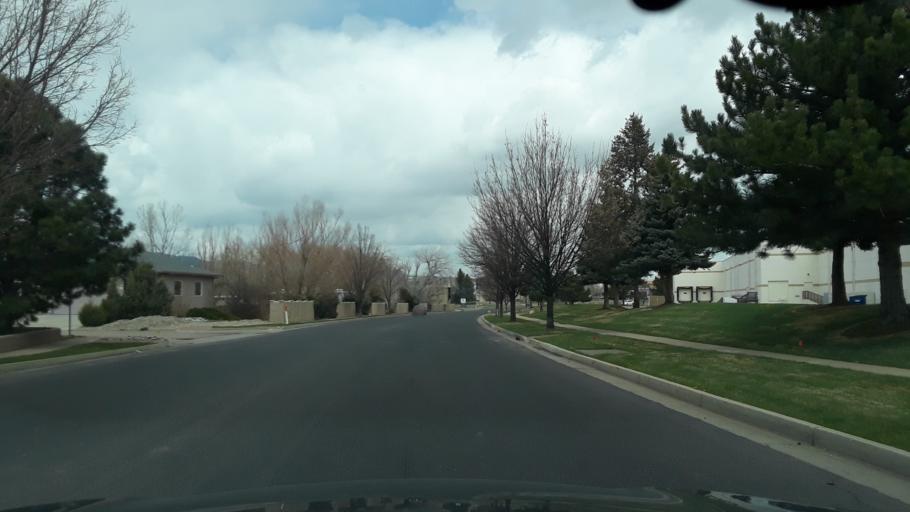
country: US
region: Colorado
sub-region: El Paso County
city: Air Force Academy
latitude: 38.9424
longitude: -104.8031
